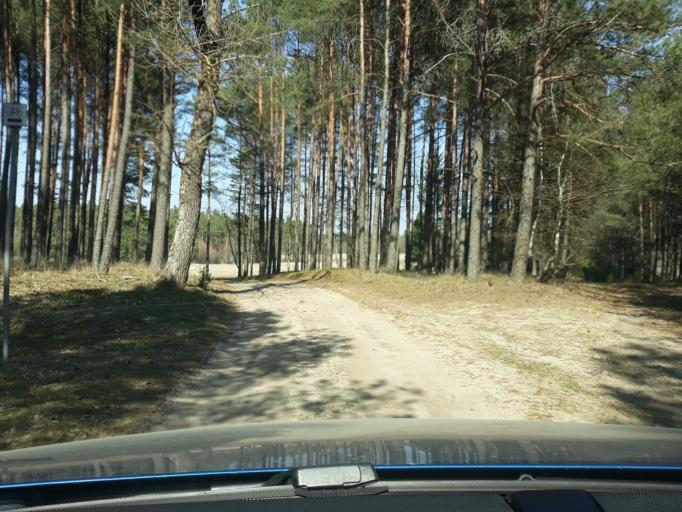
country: PL
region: Pomeranian Voivodeship
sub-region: Powiat bytowski
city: Lipnica
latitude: 53.8557
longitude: 17.4342
